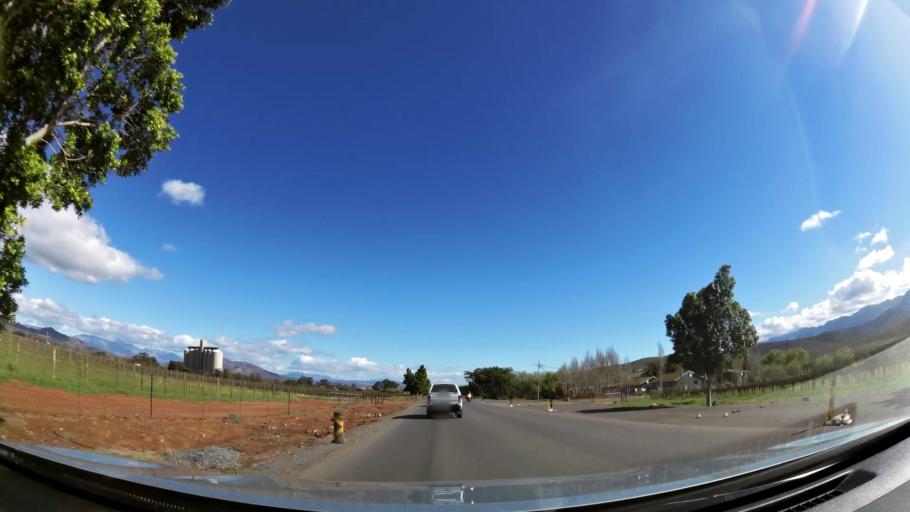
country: ZA
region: Western Cape
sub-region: Cape Winelands District Municipality
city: Ashton
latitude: -33.8313
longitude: 20.0768
